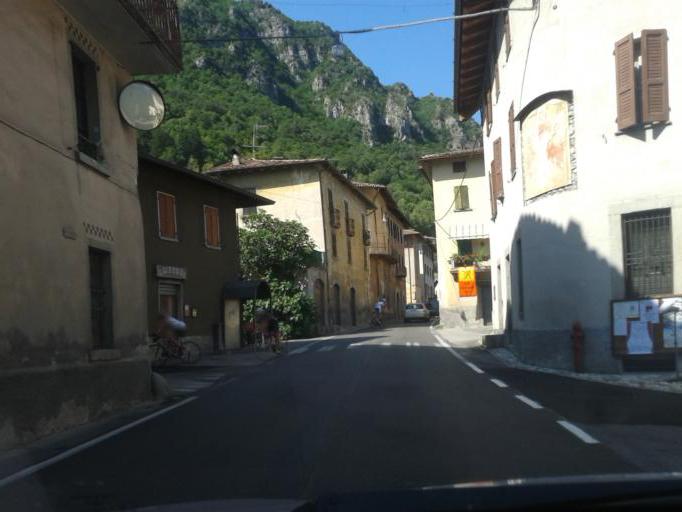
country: IT
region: Lombardy
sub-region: Provincia di Brescia
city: Anfo
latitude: 45.7660
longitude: 10.4919
